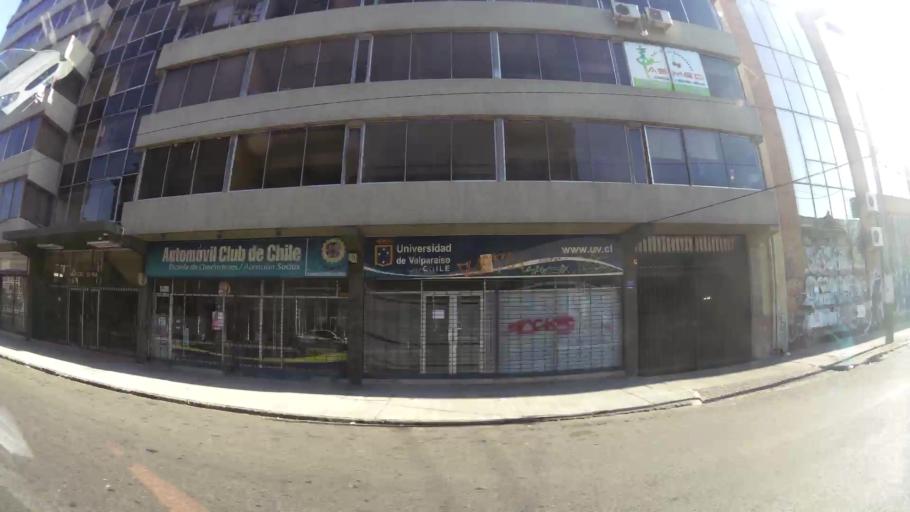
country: CL
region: Valparaiso
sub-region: Provincia de Valparaiso
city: Valparaiso
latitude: -33.0454
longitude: -71.6186
